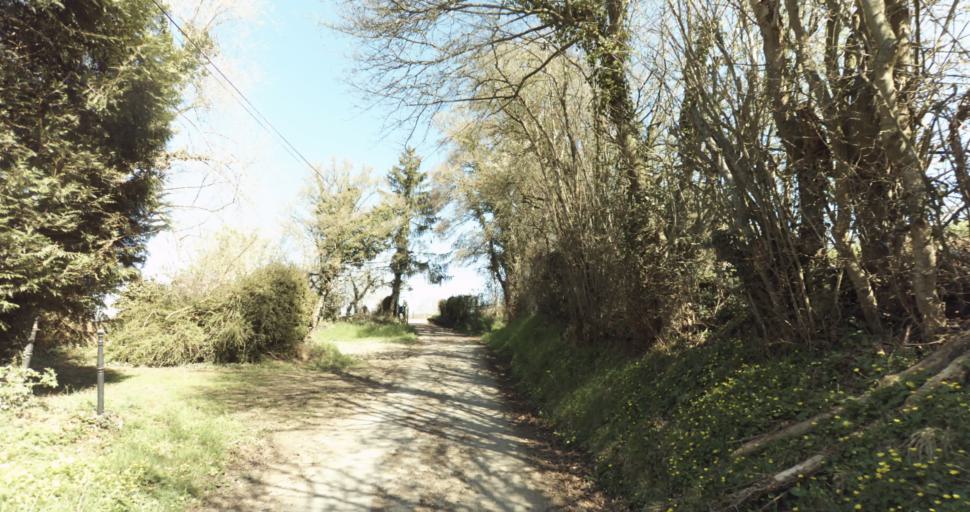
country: FR
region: Lower Normandy
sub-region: Departement du Calvados
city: Saint-Pierre-sur-Dives
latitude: 48.9938
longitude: 0.0363
